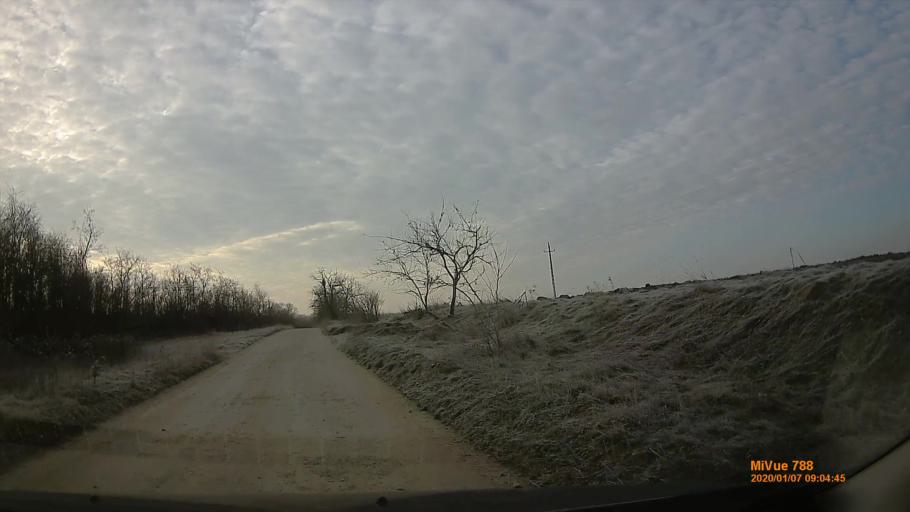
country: HU
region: Gyor-Moson-Sopron
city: Rajka
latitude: 47.9836
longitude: 17.1895
